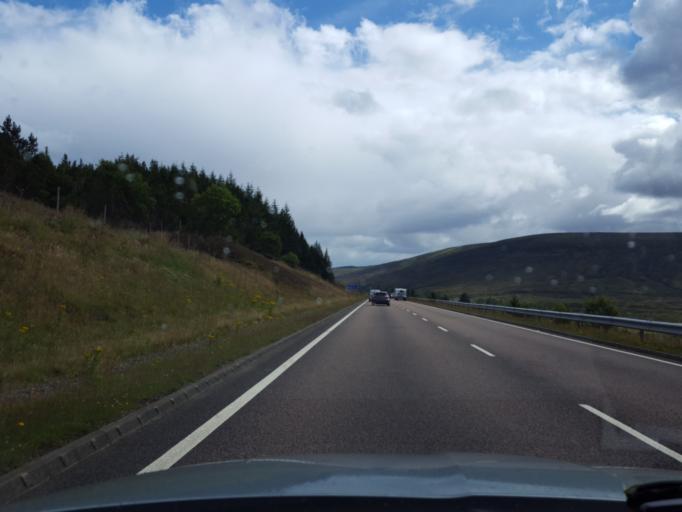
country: GB
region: Scotland
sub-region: Highland
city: Kingussie
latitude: 56.8367
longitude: -4.2303
